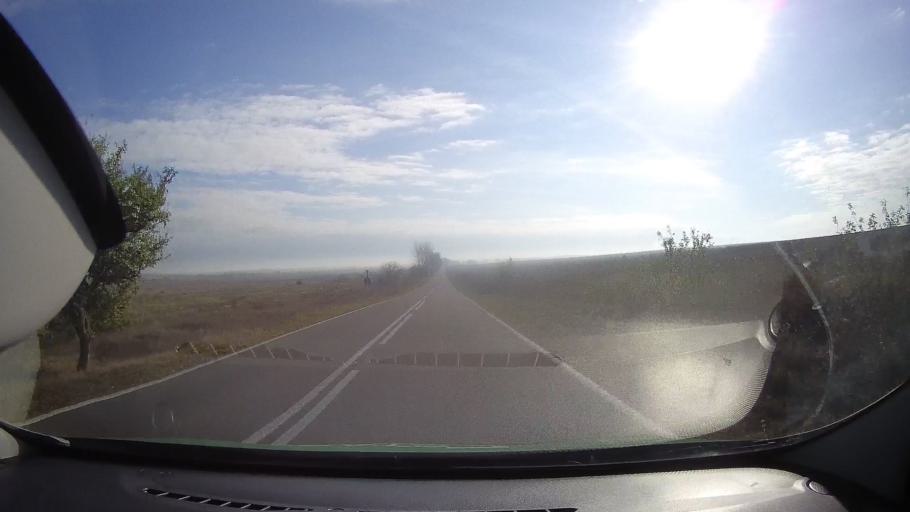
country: RO
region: Tulcea
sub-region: Comuna Mahmudia
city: Mahmudia
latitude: 45.0720
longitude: 29.0941
